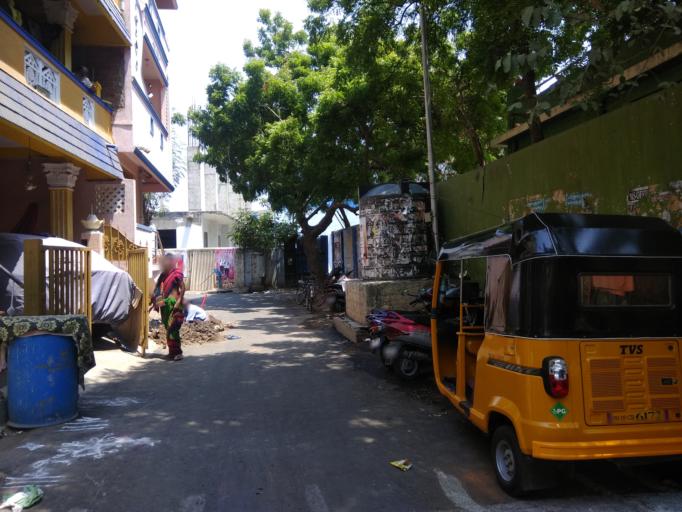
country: IN
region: Tamil Nadu
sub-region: Kancheepuram
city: Alandur
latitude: 13.0298
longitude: 80.2229
